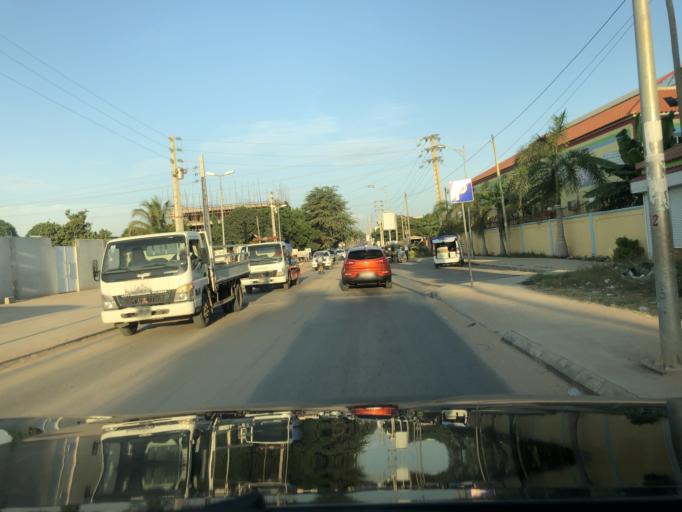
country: AO
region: Luanda
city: Luanda
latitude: -8.9497
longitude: 13.1702
